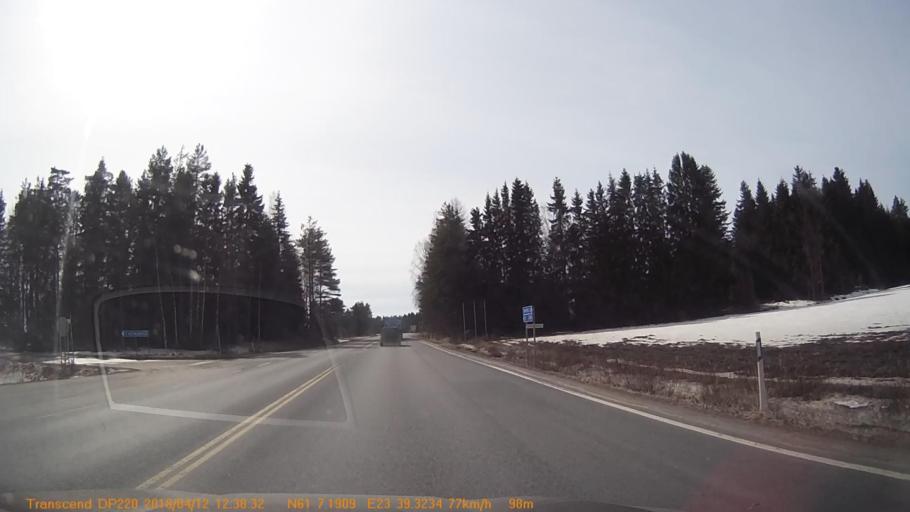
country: FI
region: Pirkanmaa
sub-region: Etelae-Pirkanmaa
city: Kylmaekoski
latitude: 61.1200
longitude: 23.6557
